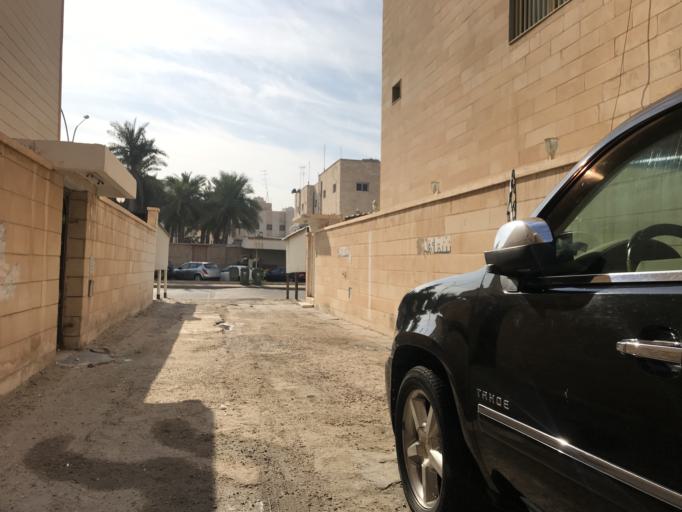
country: KW
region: Muhafazat Hawalli
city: Ar Rumaythiyah
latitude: 29.3033
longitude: 48.0746
